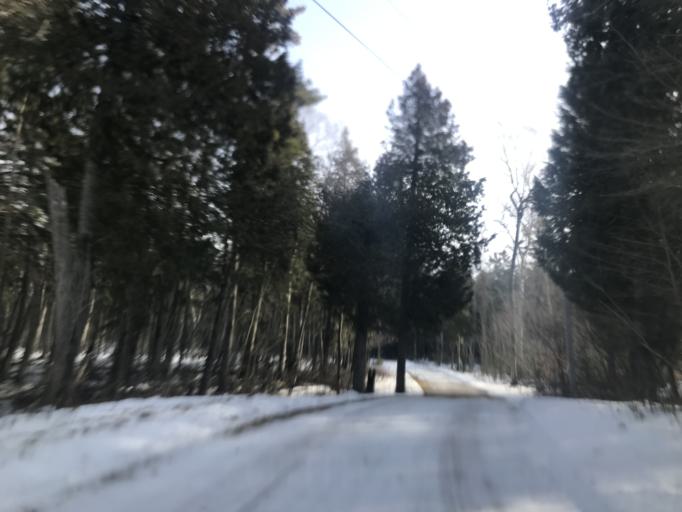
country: US
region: Wisconsin
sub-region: Door County
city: Sturgeon Bay
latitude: 45.1524
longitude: -87.0408
